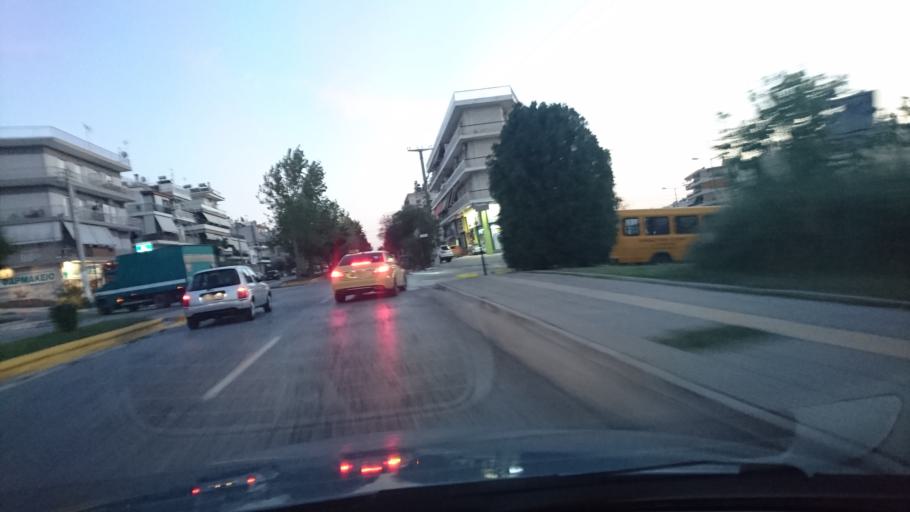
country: GR
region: Attica
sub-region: Nomarchia Athinas
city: Argyroupoli
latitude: 37.9232
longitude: 23.7509
